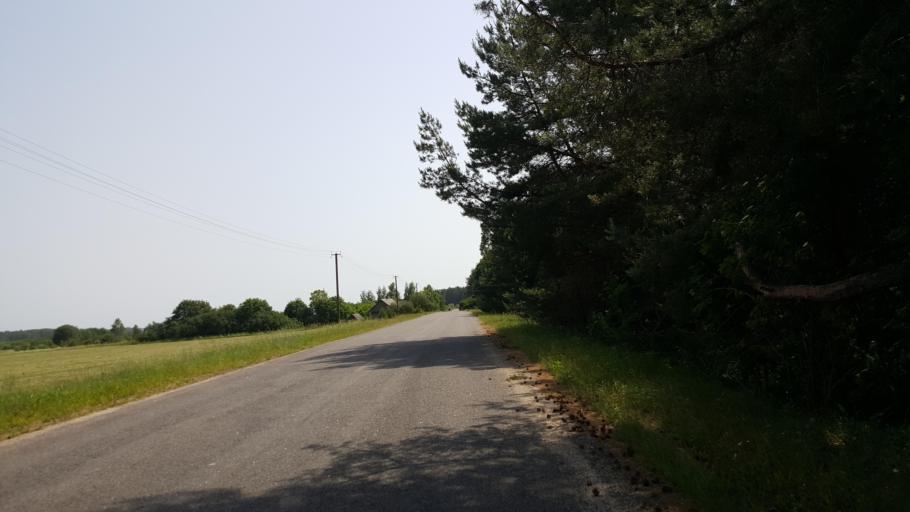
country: BY
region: Brest
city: Kamyanyuki
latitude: 52.5205
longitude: 23.8490
